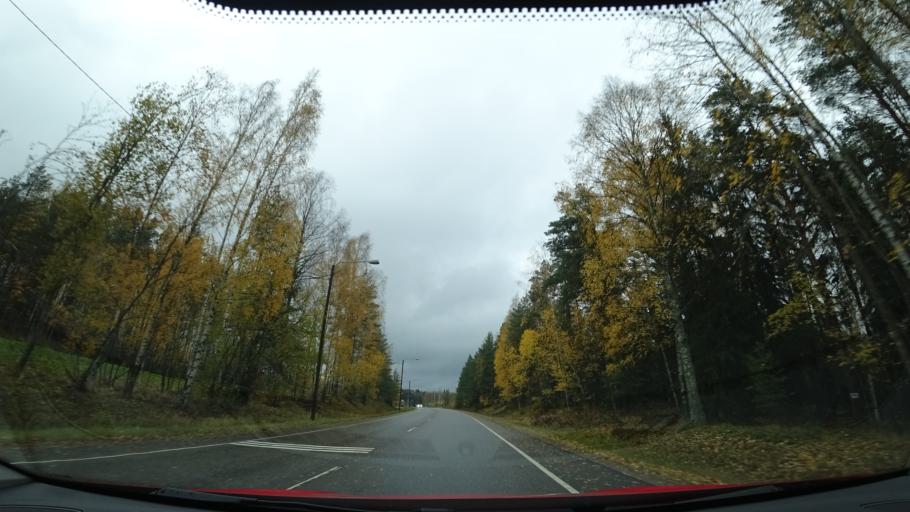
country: FI
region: Uusimaa
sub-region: Helsinki
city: Sibbo
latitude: 60.2635
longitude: 25.2107
